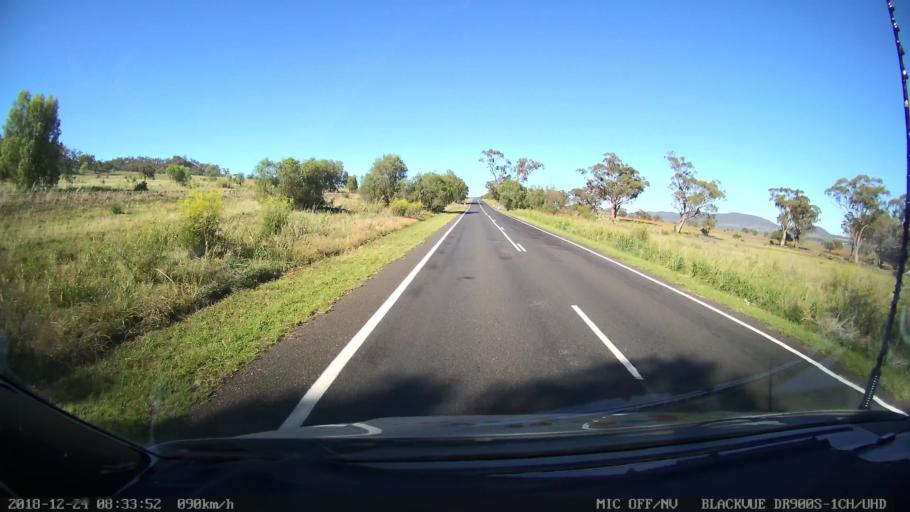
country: AU
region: New South Wales
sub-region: Liverpool Plains
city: Quirindi
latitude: -31.2890
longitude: 150.6786
